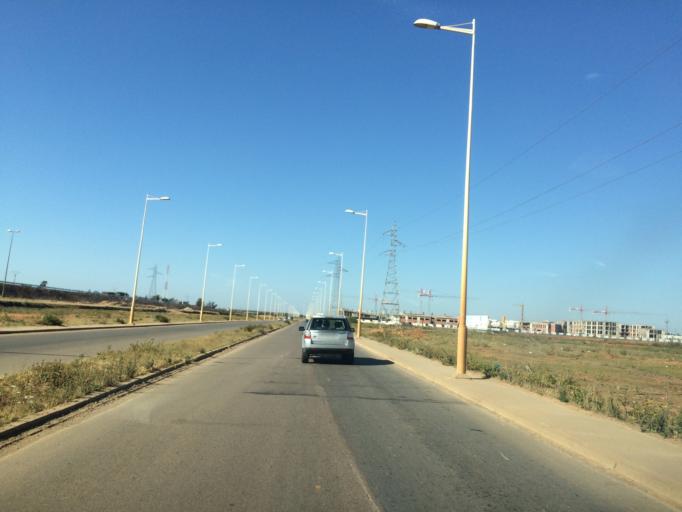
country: MA
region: Rabat-Sale-Zemmour-Zaer
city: Sale
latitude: 33.9846
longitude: -6.7305
